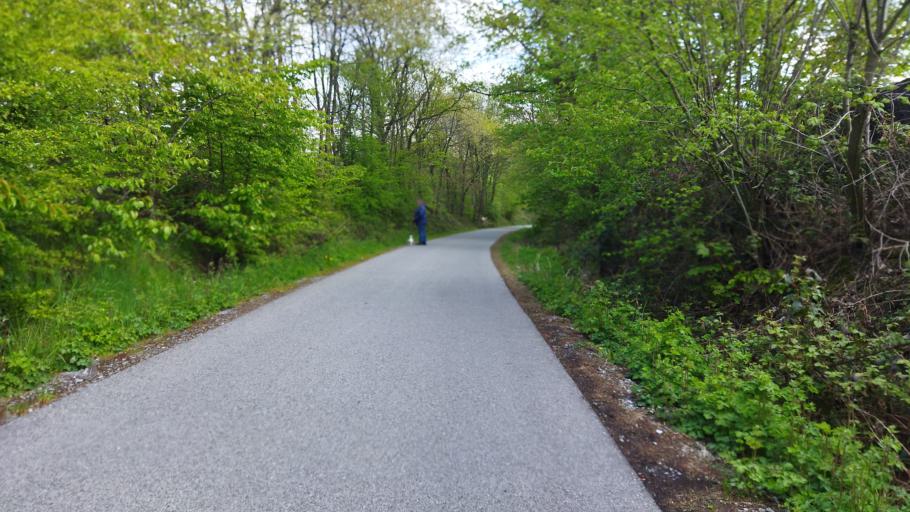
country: DE
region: North Rhine-Westphalia
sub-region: Regierungsbezirk Dusseldorf
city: Heiligenhaus
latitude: 51.3314
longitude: 7.0002
